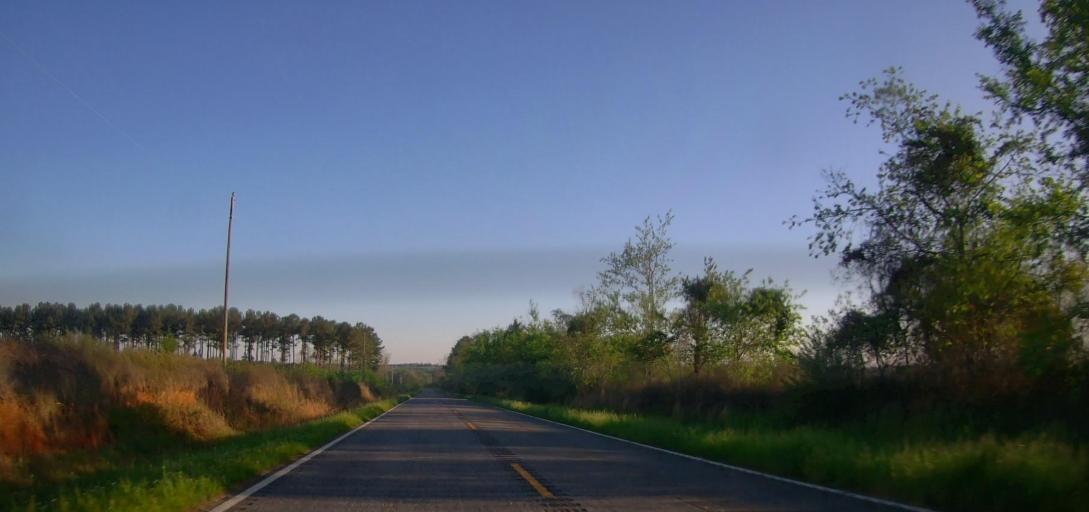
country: US
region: Georgia
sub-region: Marion County
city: Buena Vista
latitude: 32.3936
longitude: -84.4431
